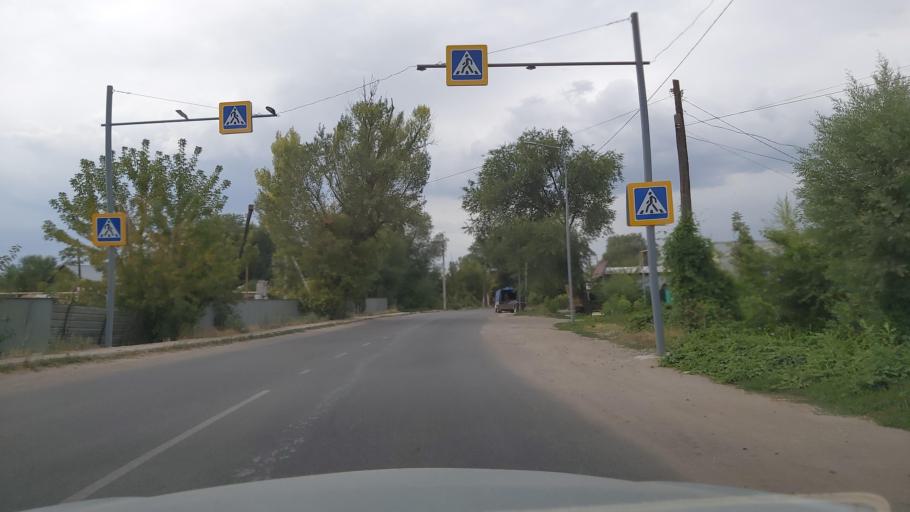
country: KZ
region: Almaty Oblysy
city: Energeticheskiy
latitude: 43.3885
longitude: 77.0748
